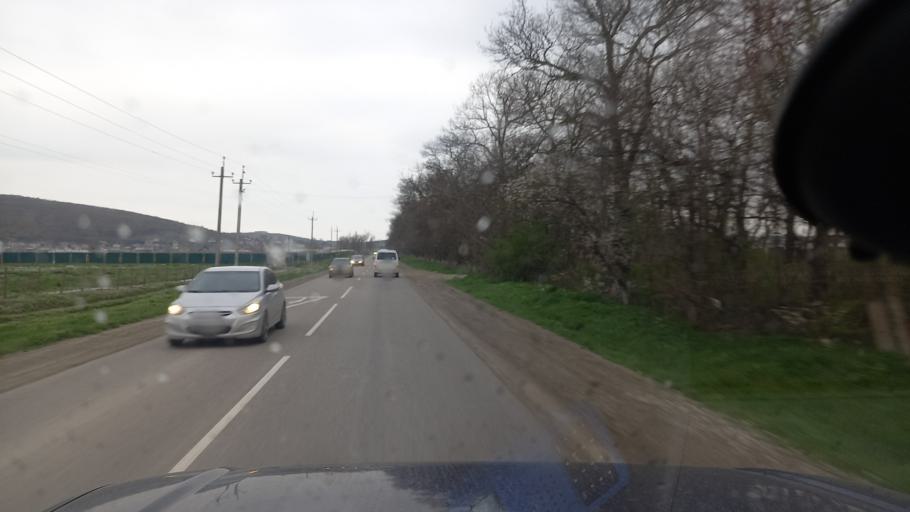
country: RU
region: Krasnodarskiy
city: Anapskaya
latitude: 44.8691
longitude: 37.4429
